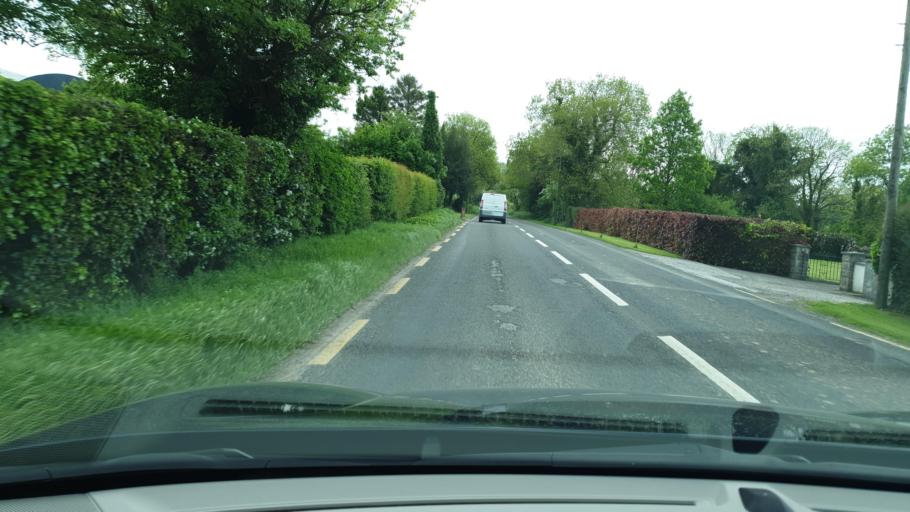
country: IE
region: Leinster
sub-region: An Mhi
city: Navan
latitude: 53.7207
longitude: -6.6998
